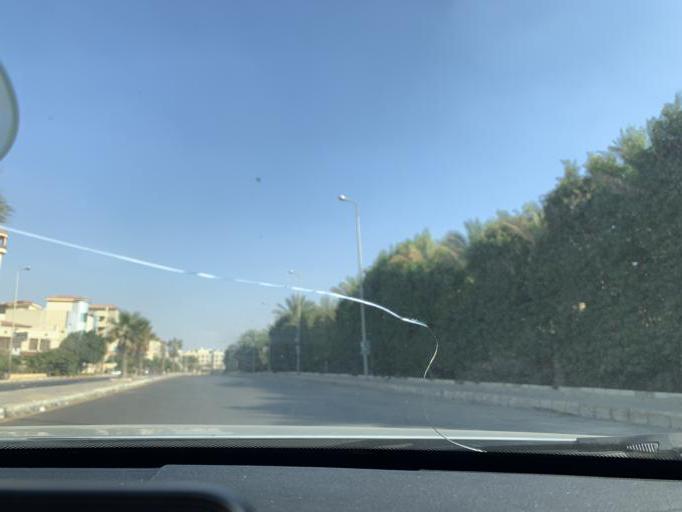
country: EG
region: Muhafazat al Qalyubiyah
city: Al Khankah
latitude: 30.0187
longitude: 31.4816
